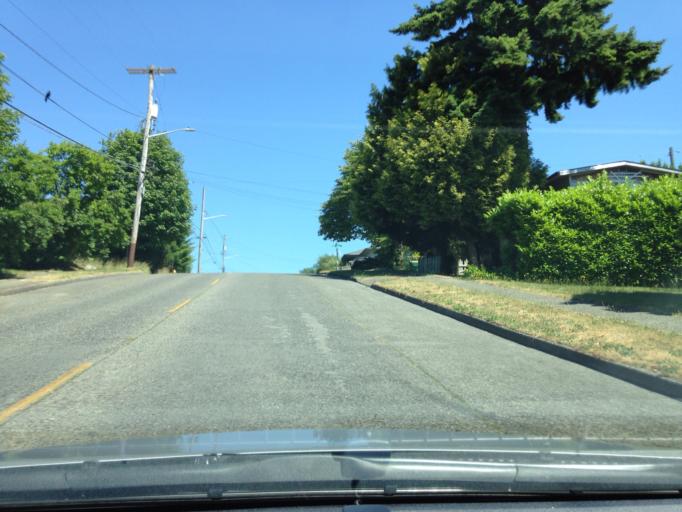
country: US
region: Washington
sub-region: King County
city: Mercer Island
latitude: 47.5512
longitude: -122.2858
